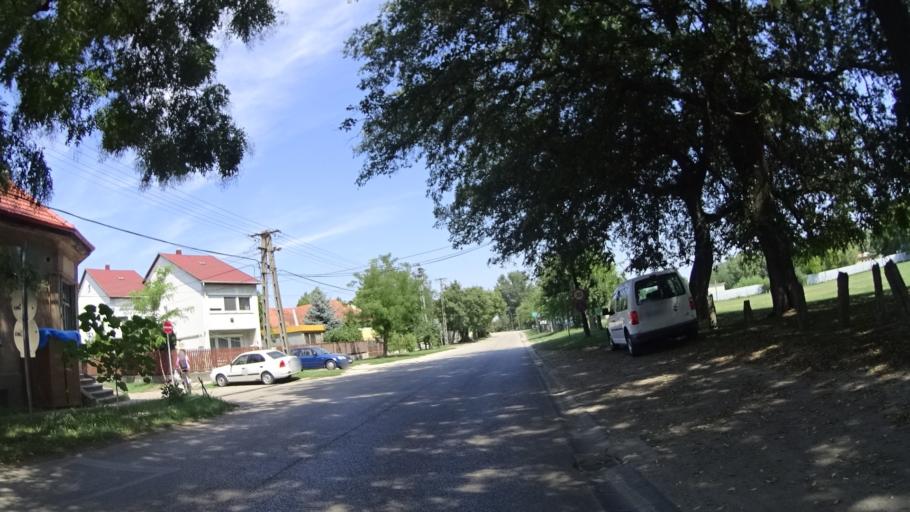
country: HU
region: Fejer
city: Szekesfehervar
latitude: 47.1698
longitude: 18.4092
